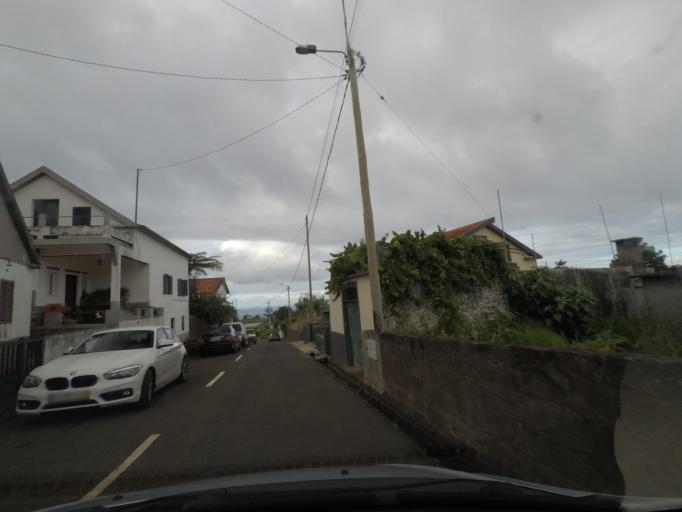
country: PT
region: Madeira
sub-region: Santana
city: Santana
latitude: 32.8129
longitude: -16.8792
